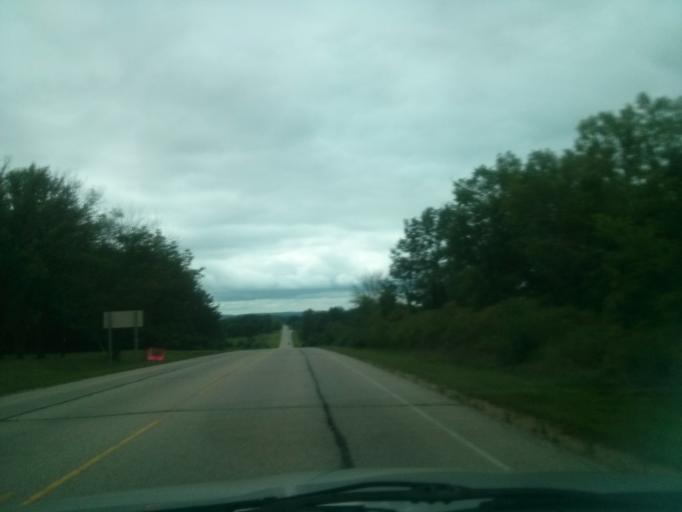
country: US
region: Wisconsin
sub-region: Pierce County
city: Spring Valley
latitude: 44.8321
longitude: -92.3389
